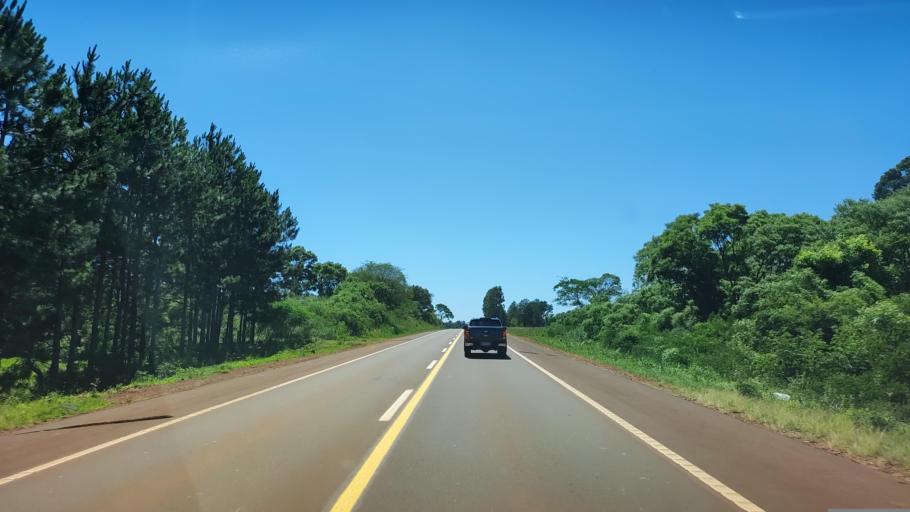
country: AR
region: Misiones
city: Aristobulo del Valle
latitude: -27.0861
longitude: -54.7955
